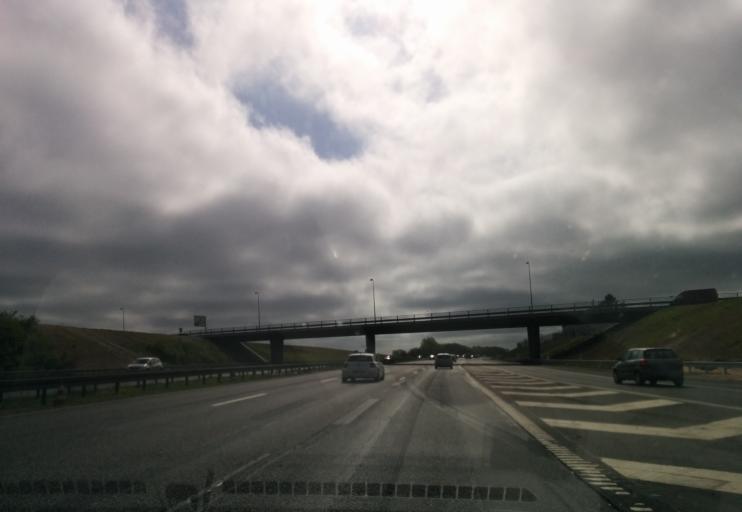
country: DK
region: South Denmark
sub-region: Middelfart Kommune
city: Strib
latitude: 55.5137
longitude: 9.7719
